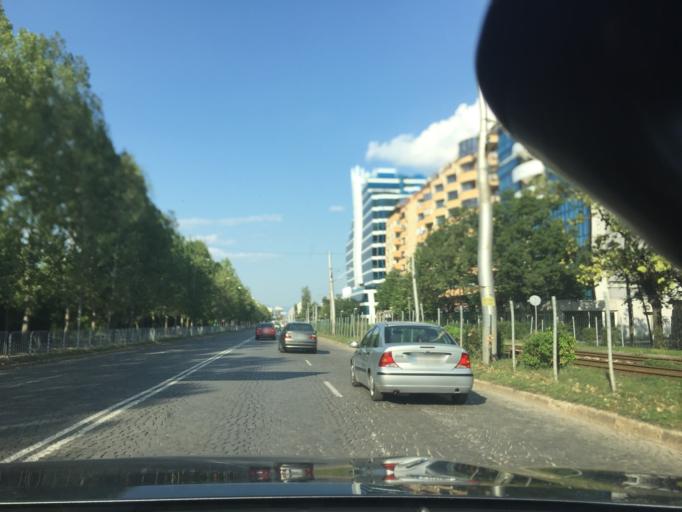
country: BG
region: Sofia-Capital
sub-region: Stolichna Obshtina
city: Sofia
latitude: 42.6729
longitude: 23.2745
